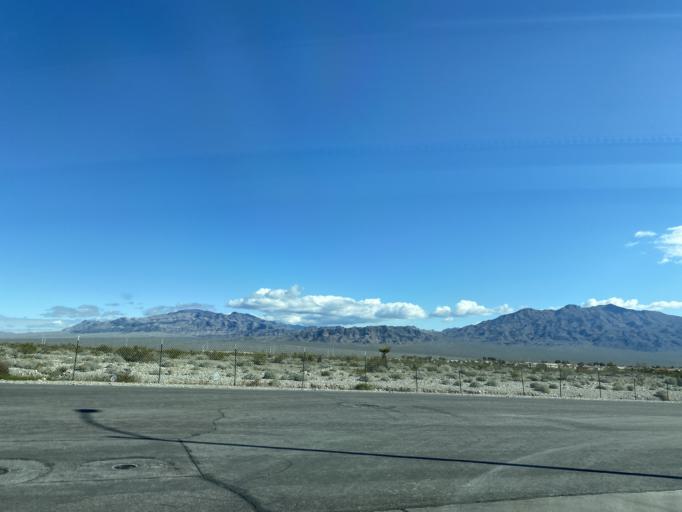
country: US
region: Nevada
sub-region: Clark County
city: Summerlin South
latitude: 36.3213
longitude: -115.3014
